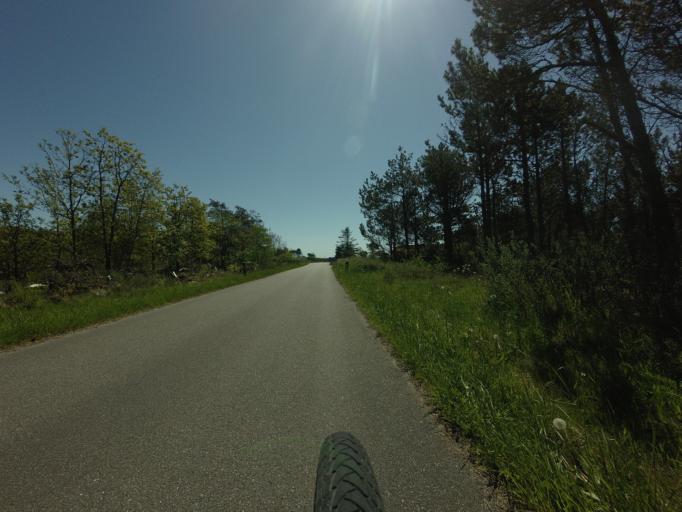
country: DK
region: North Denmark
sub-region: Jammerbugt Kommune
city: Kas
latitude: 57.2209
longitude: 9.5763
